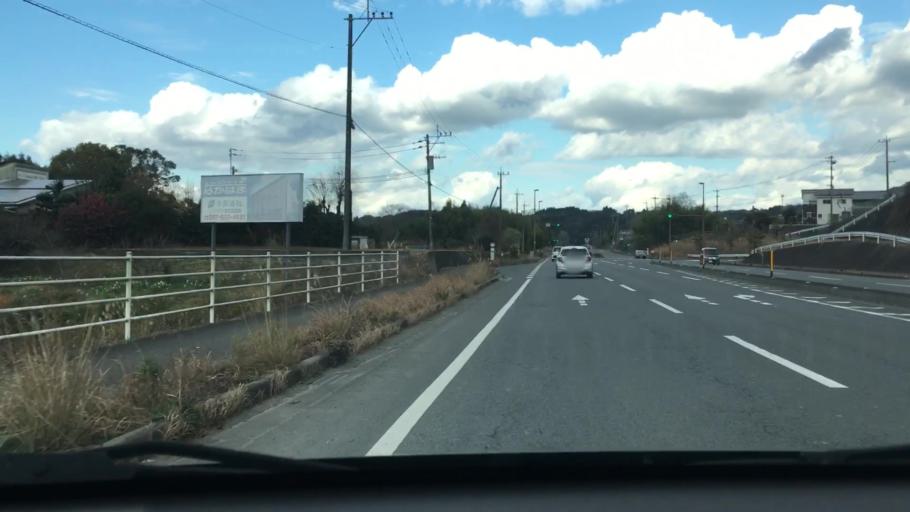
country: JP
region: Oita
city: Oita
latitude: 33.1260
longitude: 131.6556
